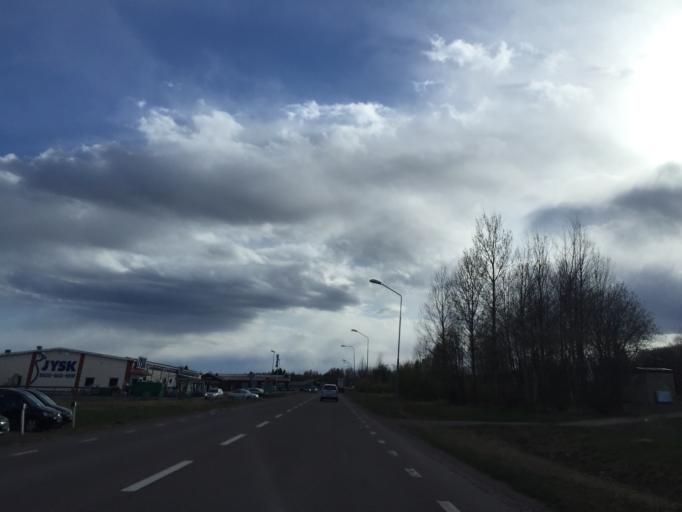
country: SE
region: Dalarna
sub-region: Borlange Kommun
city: Borlaenge
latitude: 60.4722
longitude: 15.4007
